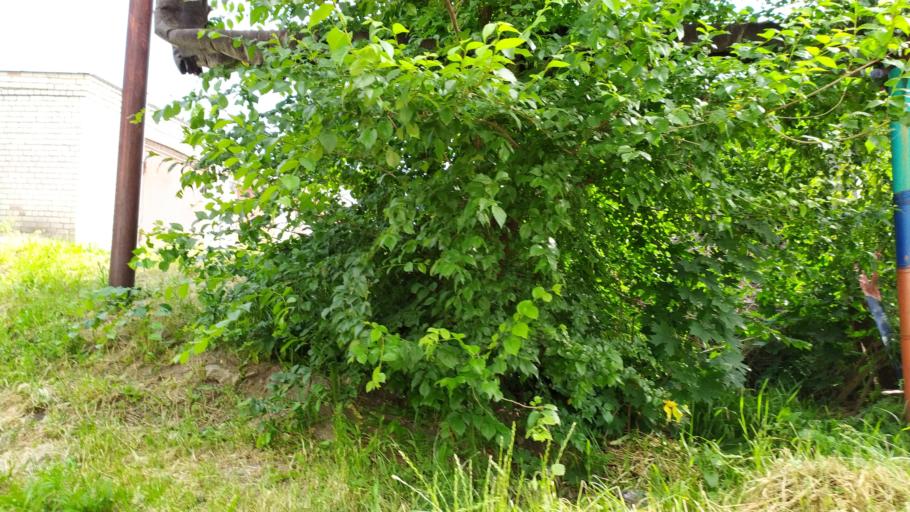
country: RU
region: Kursk
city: Kursk
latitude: 51.6637
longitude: 36.1518
